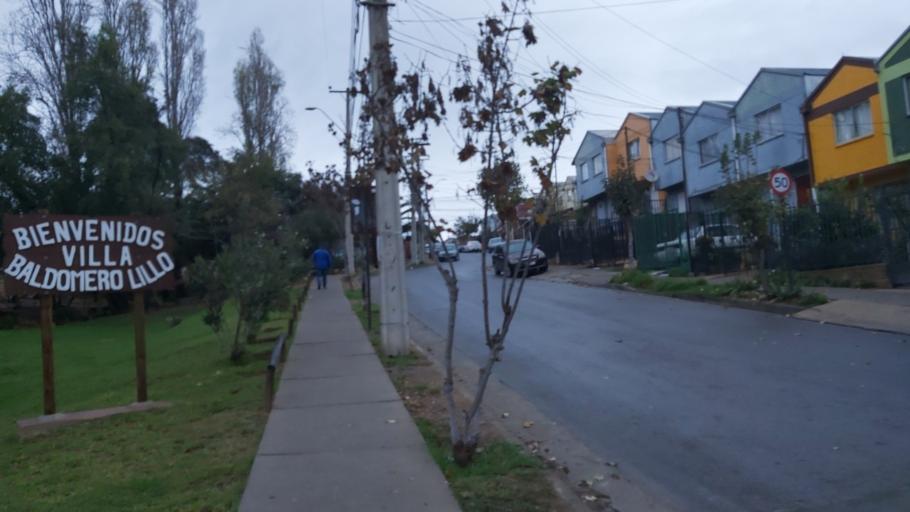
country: CL
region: Valparaiso
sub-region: Provincia de Marga Marga
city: Quilpue
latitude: -33.0523
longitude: -71.4209
